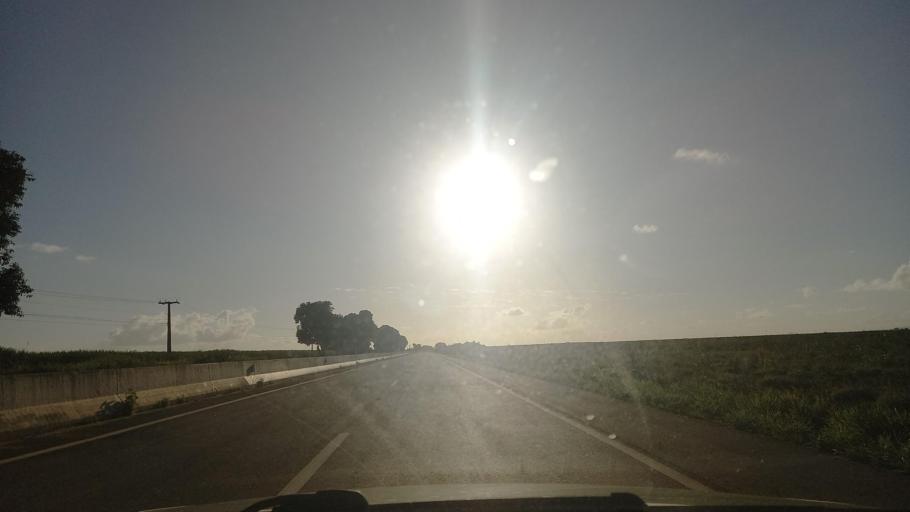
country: BR
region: Alagoas
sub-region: Campo Alegre
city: Campo Alegre
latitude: -9.7948
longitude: -36.3079
